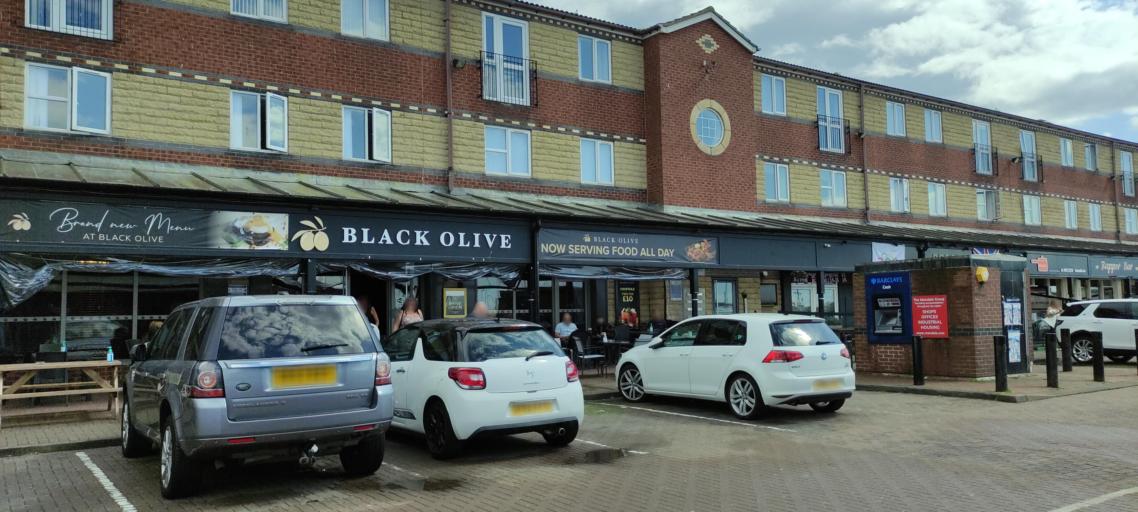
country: GB
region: England
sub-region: Hartlepool
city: Hartlepool
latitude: 54.6922
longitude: -1.1987
